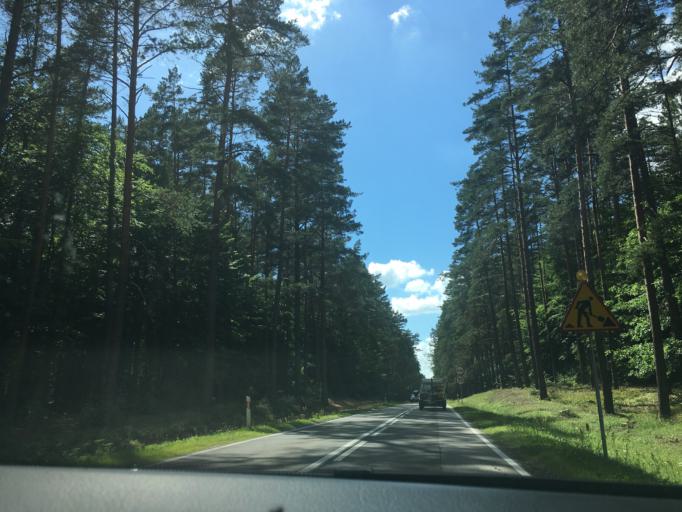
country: PL
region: Podlasie
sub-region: Powiat augustowski
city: Augustow
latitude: 53.8560
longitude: 23.0735
